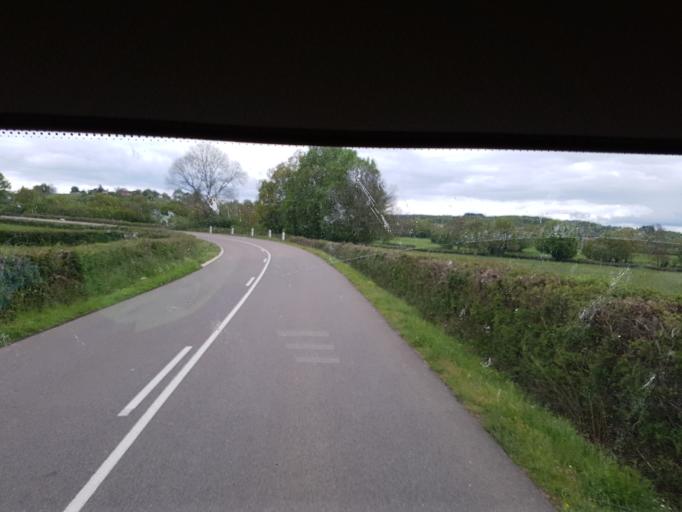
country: FR
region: Bourgogne
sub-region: Departement de Saone-et-Loire
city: Charolles
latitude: 46.4835
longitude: 4.2775
